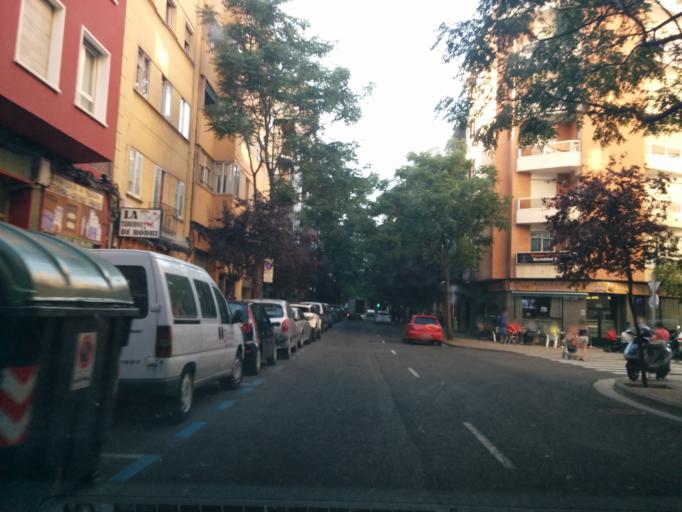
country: ES
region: Aragon
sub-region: Provincia de Zaragoza
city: Delicias
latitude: 41.6497
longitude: -0.9008
